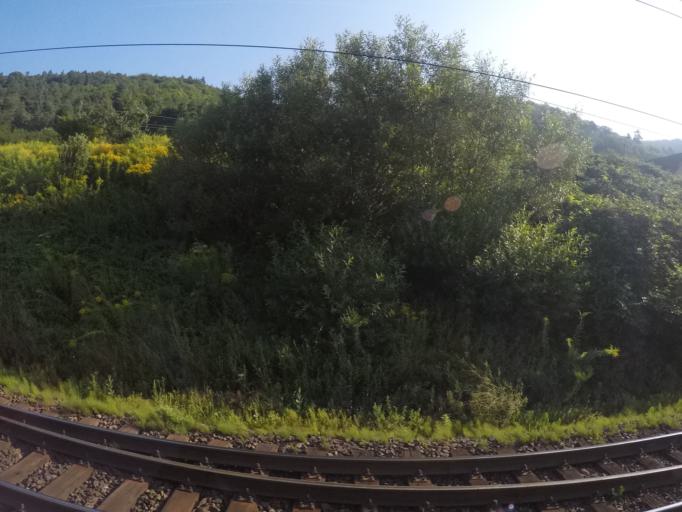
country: SK
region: Kosicky
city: Gelnica
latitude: 48.8913
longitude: 21.0356
